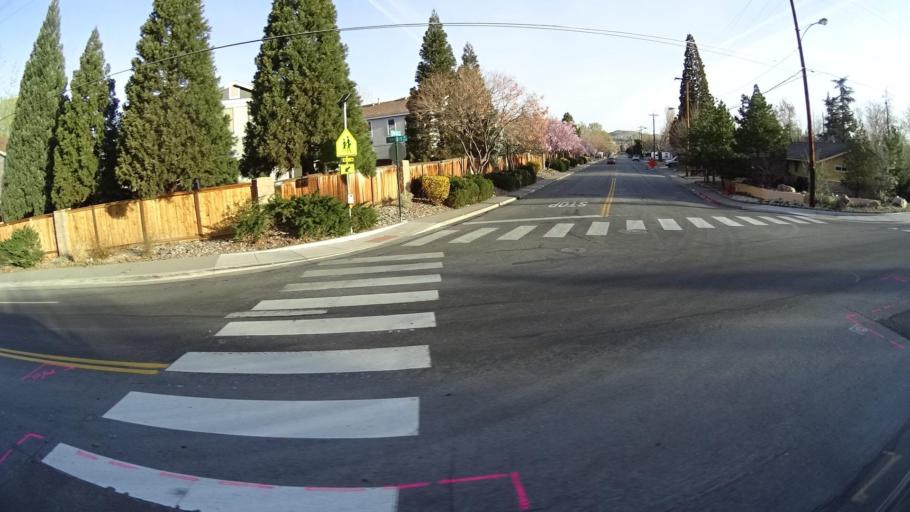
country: US
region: Nevada
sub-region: Washoe County
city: Reno
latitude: 39.5067
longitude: -119.8465
